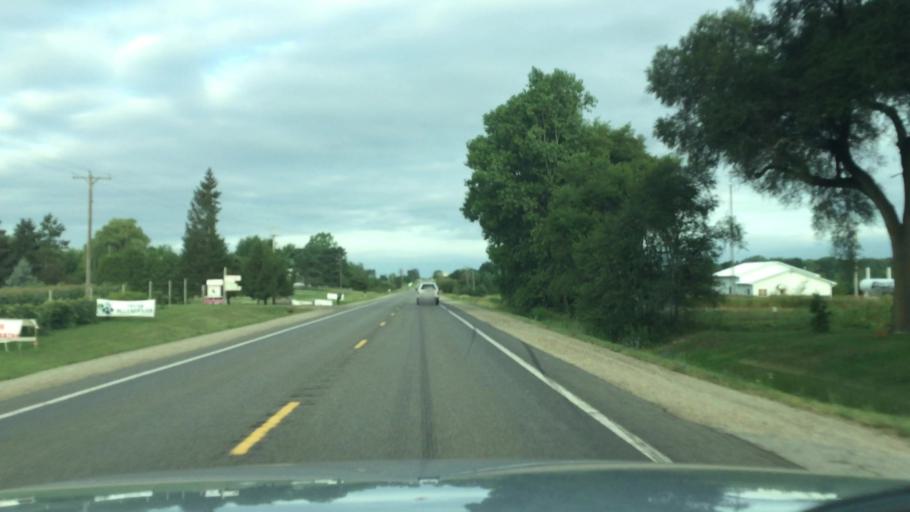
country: US
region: Michigan
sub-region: Montcalm County
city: Carson City
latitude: 43.1776
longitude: -84.9448
